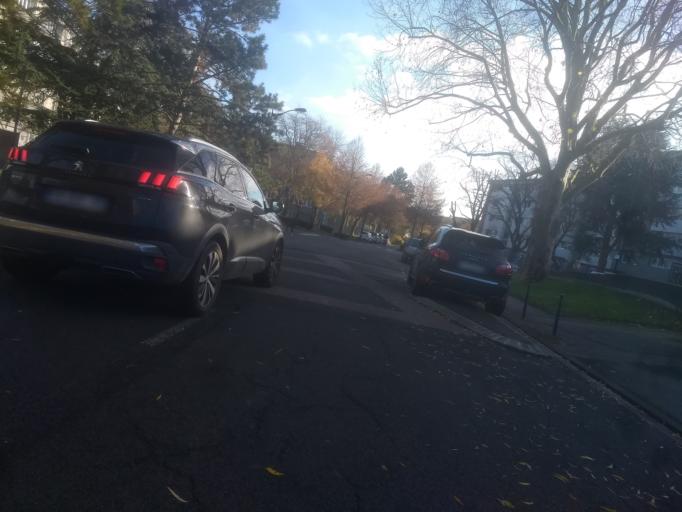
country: FR
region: Nord-Pas-de-Calais
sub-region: Departement du Pas-de-Calais
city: Anzin-Saint-Aubin
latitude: 50.3007
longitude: 2.7471
